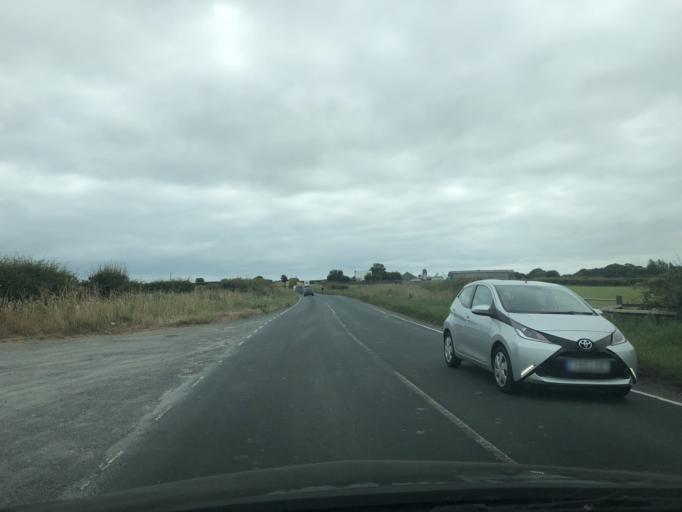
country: GB
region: England
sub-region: North Yorkshire
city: Hunmanby
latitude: 54.2298
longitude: -0.3537
